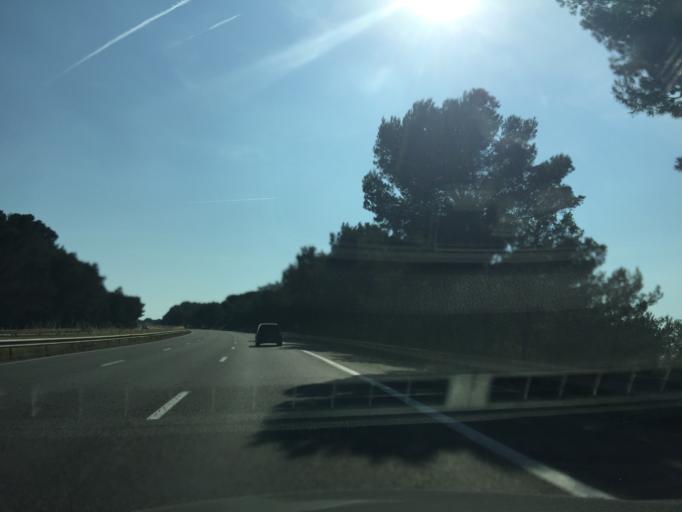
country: FR
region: Provence-Alpes-Cote d'Azur
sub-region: Departement des Bouches-du-Rhone
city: Martigues
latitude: 43.3975
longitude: 5.0726
